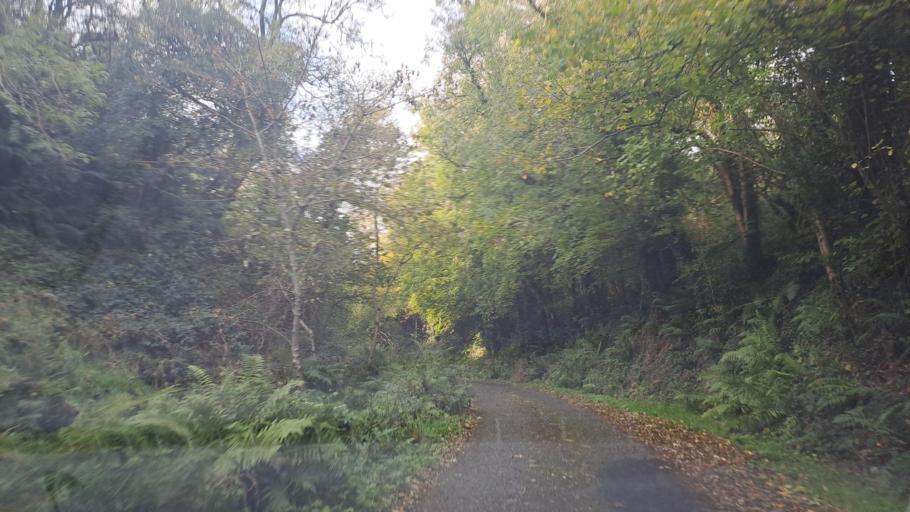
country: IE
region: Ulster
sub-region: An Cabhan
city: Kingscourt
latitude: 54.0027
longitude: -6.8179
